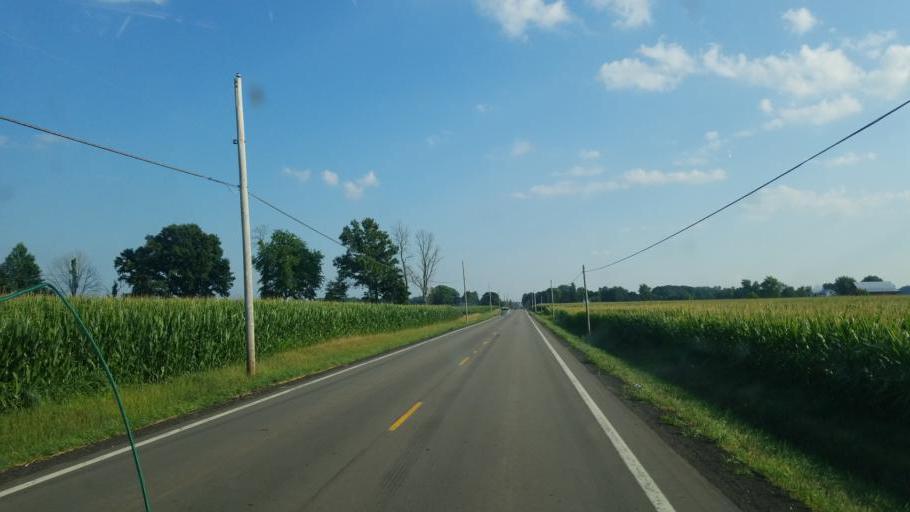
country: US
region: Ohio
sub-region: Crawford County
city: Galion
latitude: 40.7791
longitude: -82.8573
